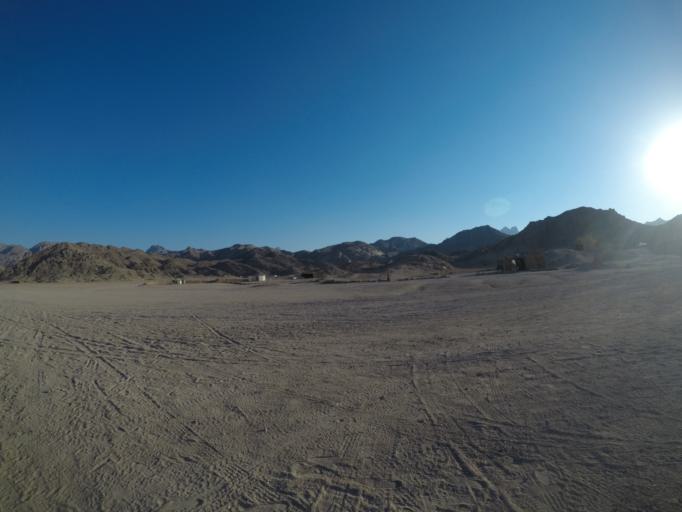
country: EG
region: Red Sea
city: El Gouna
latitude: 27.1522
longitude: 33.5436
